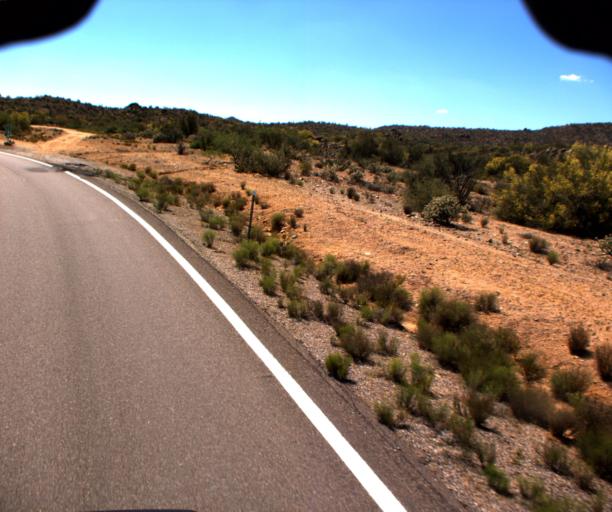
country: US
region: Arizona
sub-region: Yavapai County
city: Bagdad
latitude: 34.4606
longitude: -113.2431
